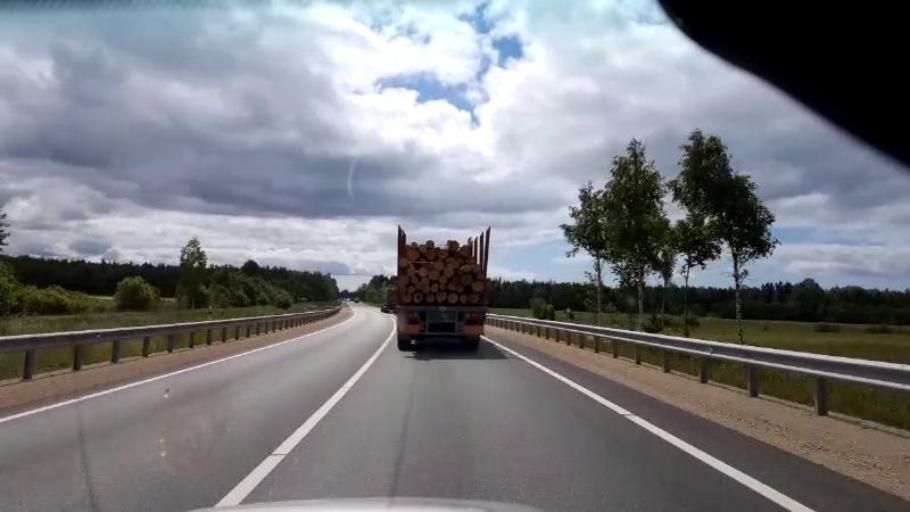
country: LV
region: Salacgrivas
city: Salacgriva
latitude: 57.7152
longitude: 24.3648
